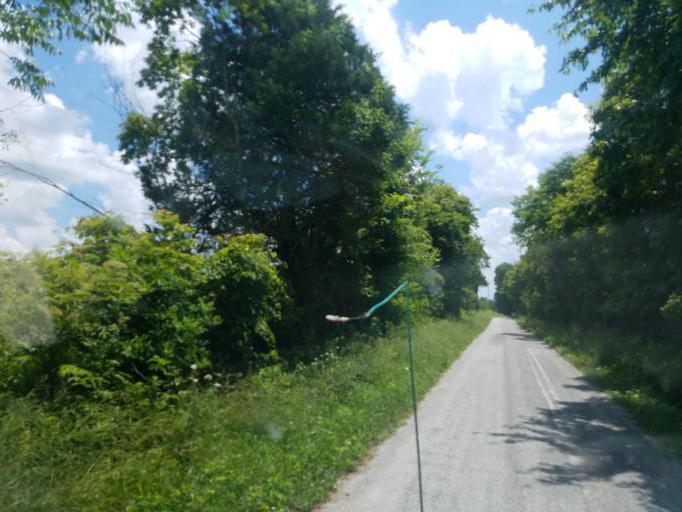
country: US
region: Kentucky
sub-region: Grayson County
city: Leitchfield
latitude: 37.4803
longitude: -86.4616
